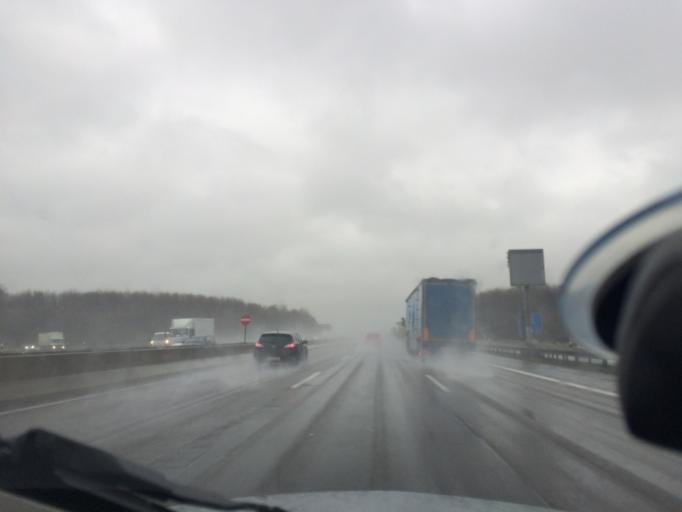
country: DE
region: Hesse
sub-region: Regierungsbezirk Darmstadt
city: Bad Homburg vor der Hoehe
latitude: 50.1990
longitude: 8.6420
